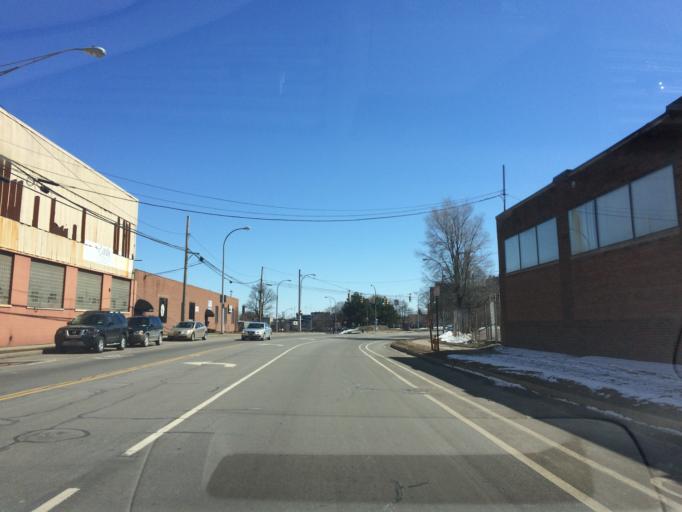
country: US
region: New York
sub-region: Monroe County
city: Brighton
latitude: 43.1501
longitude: -77.5658
